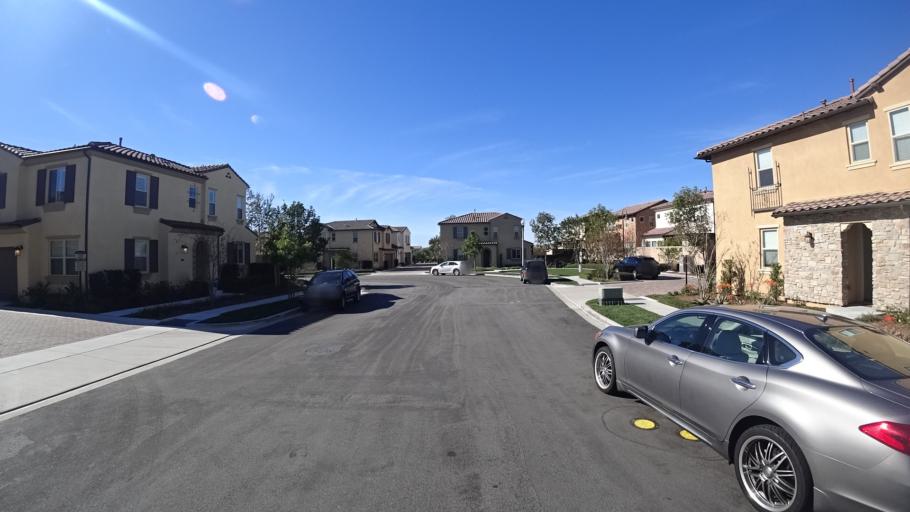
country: US
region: California
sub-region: Orange County
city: Lake Forest
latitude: 33.6721
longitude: -117.6827
